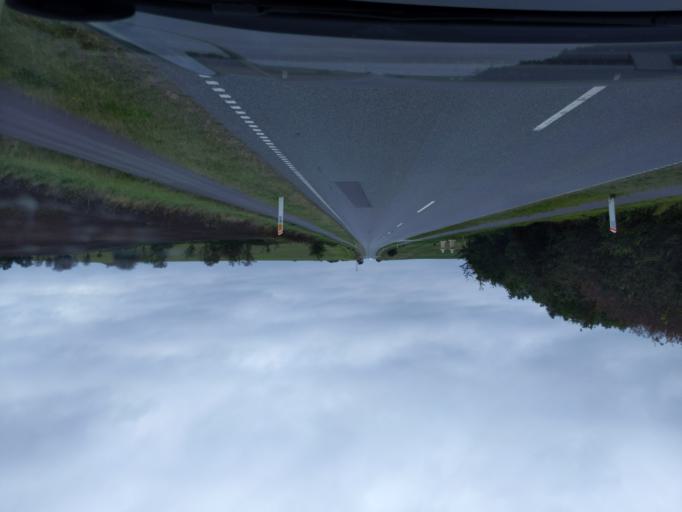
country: DK
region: North Denmark
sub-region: Mariagerfjord Kommune
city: Hobro
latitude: 56.5945
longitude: 9.7832
